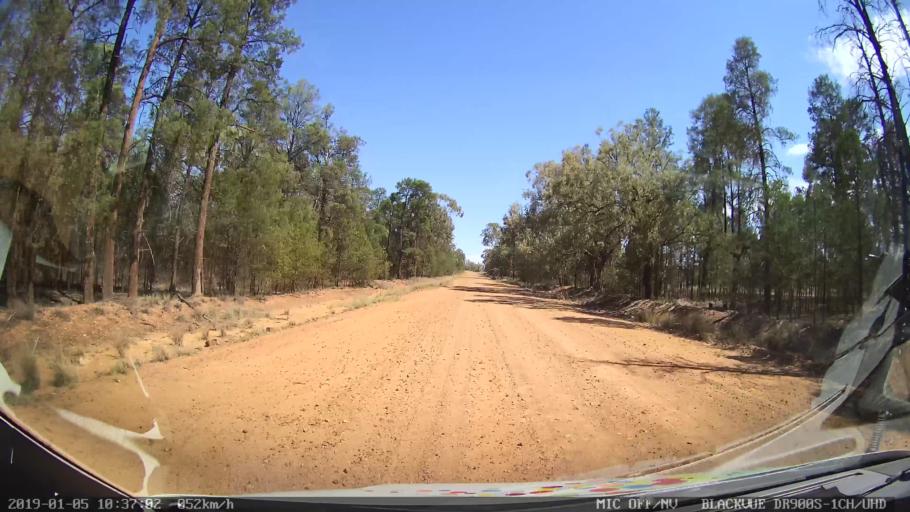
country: AU
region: New South Wales
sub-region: Gilgandra
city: Gilgandra
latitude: -31.4776
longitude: 148.9230
